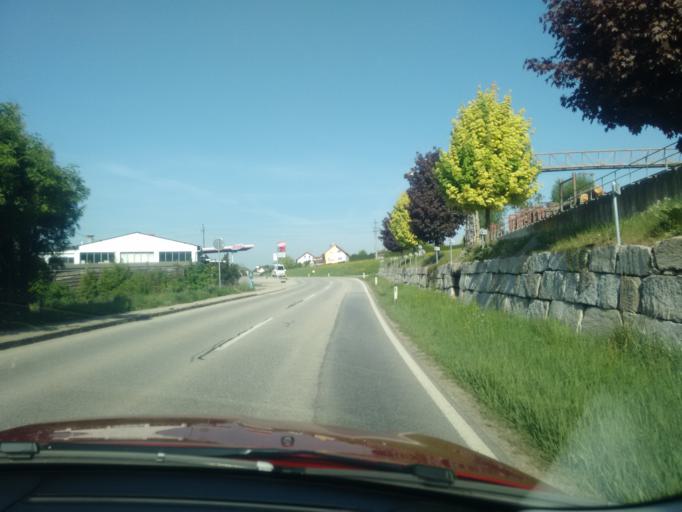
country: AT
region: Upper Austria
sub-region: Politischer Bezirk Grieskirchen
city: Bad Schallerbach
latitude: 48.2601
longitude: 13.9418
